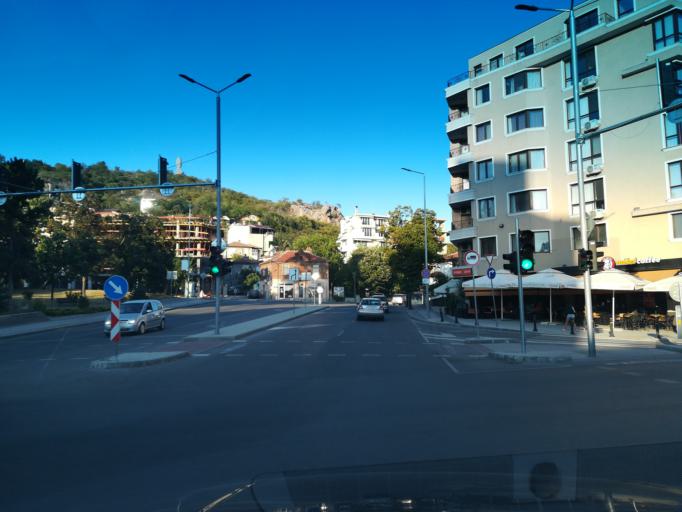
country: BG
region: Plovdiv
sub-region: Obshtina Plovdiv
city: Plovdiv
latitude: 42.1416
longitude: 24.7337
